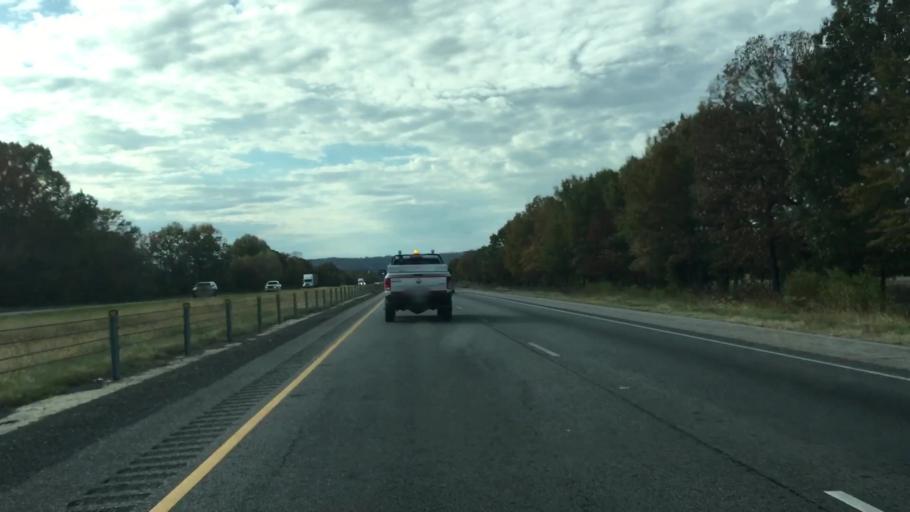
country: US
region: Arkansas
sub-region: Pope County
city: Atkins
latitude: 35.2481
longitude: -92.8742
